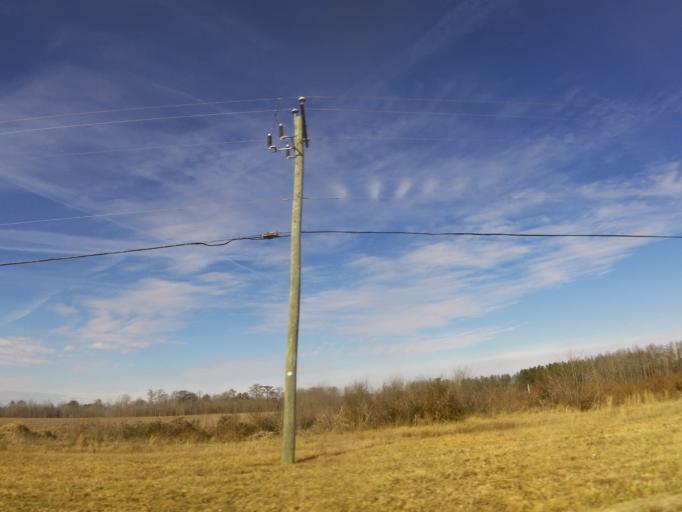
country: US
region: Virginia
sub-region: Isle of Wight County
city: Windsor
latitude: 36.7844
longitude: -76.8146
